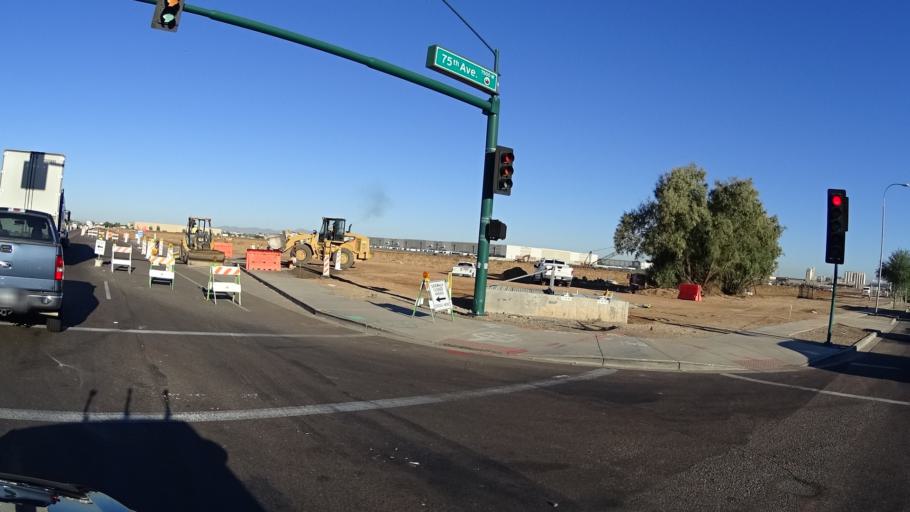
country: US
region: Arizona
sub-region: Maricopa County
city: Tolleson
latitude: 33.4372
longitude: -112.2211
